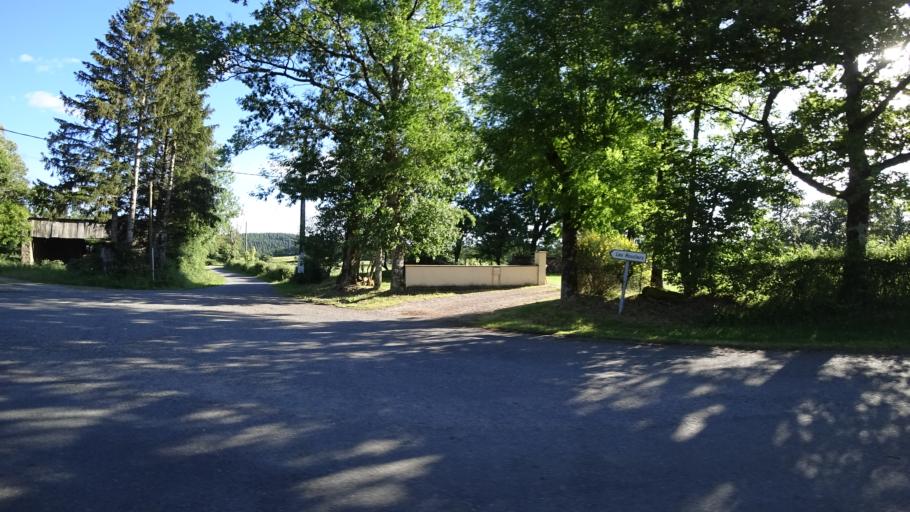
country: FR
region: Midi-Pyrenees
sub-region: Departement de l'Aveyron
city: Pont-de-Salars
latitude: 44.3114
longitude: 2.7584
